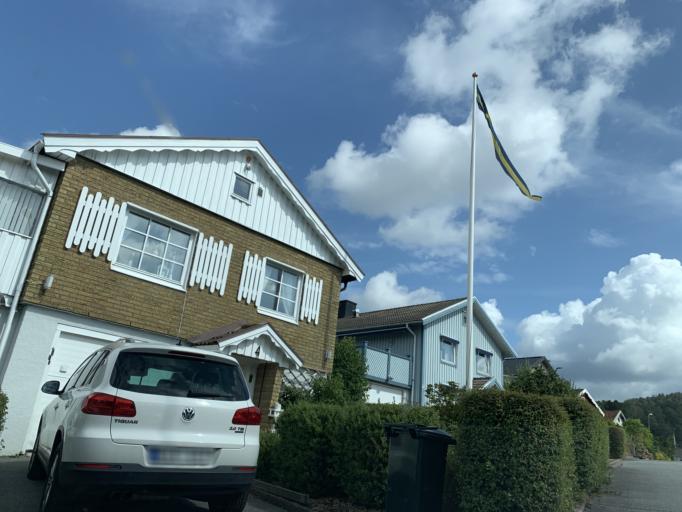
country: SE
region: Vaestra Goetaland
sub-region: Goteborg
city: Eriksbo
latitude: 57.7452
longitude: 12.0476
